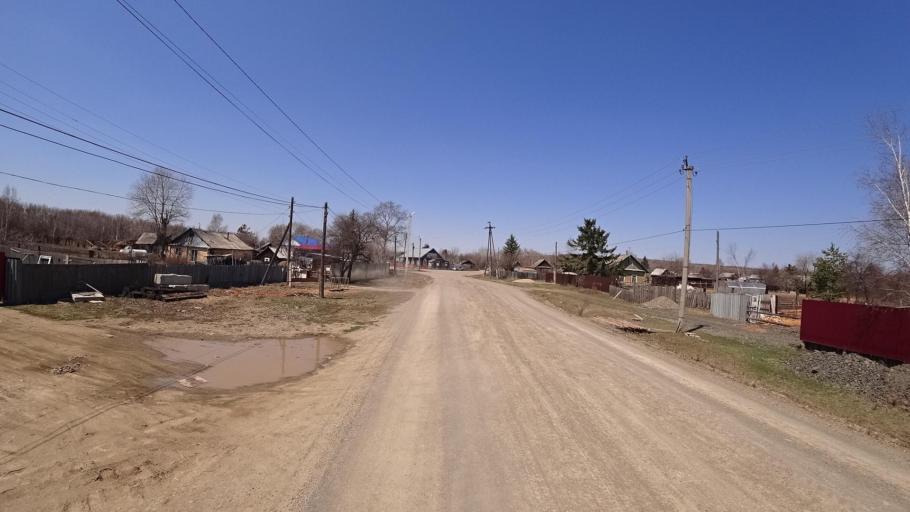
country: RU
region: Khabarovsk Krai
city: Khurba
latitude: 50.4090
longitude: 136.8664
